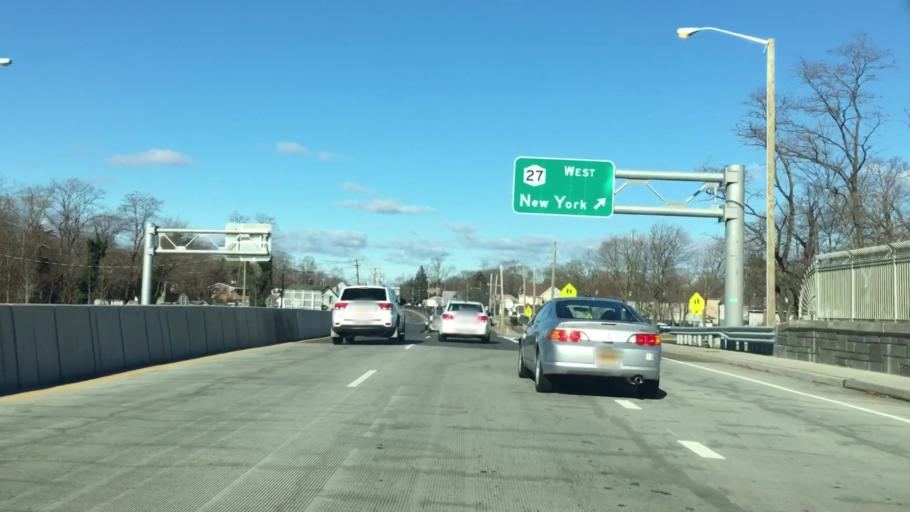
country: US
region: New York
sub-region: Suffolk County
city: Amityville
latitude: 40.6872
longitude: -73.4192
